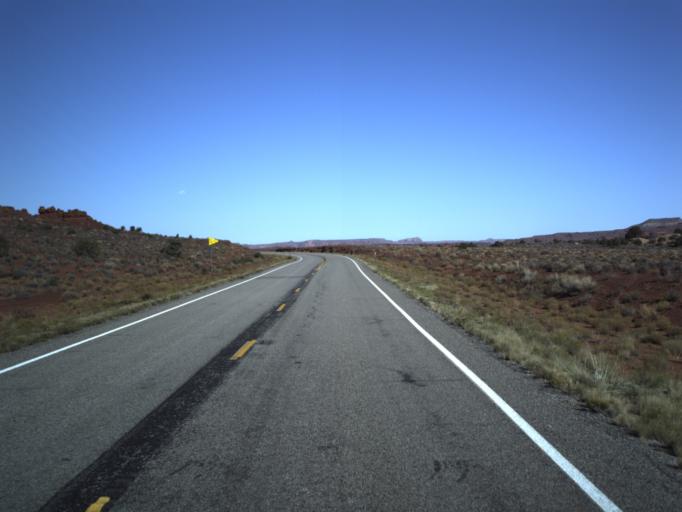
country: US
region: Utah
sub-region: San Juan County
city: Blanding
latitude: 37.7983
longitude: -110.3050
